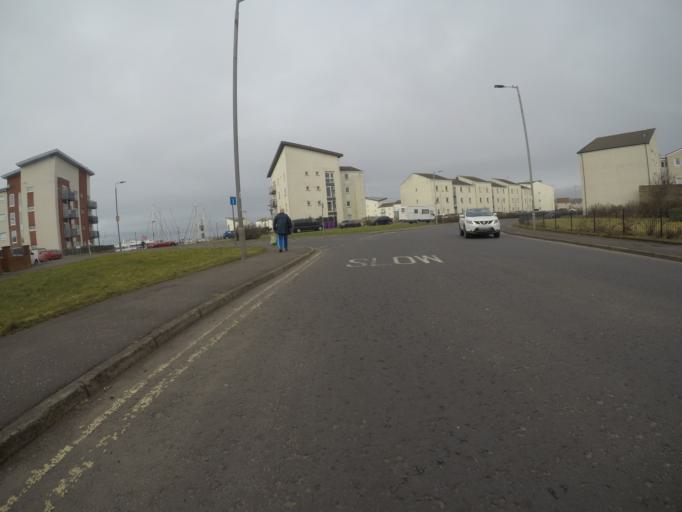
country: GB
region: Scotland
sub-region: North Ayrshire
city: Ardrossan
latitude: 55.6405
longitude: -4.8160
